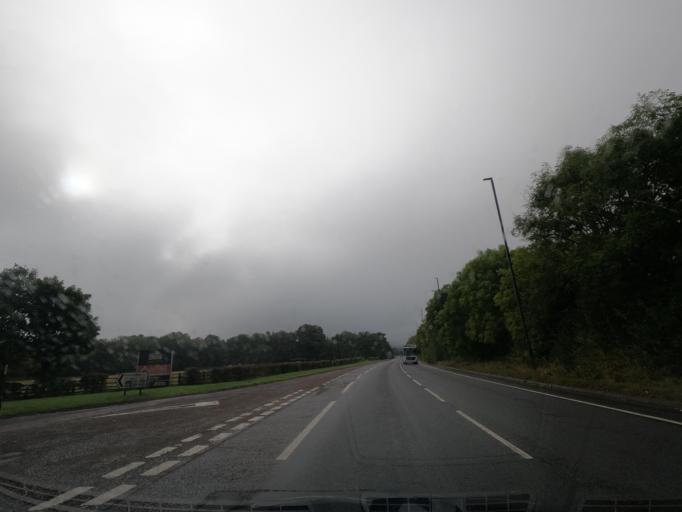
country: GB
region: England
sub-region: Redcar and Cleveland
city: Redcar
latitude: 54.5923
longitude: -1.0836
